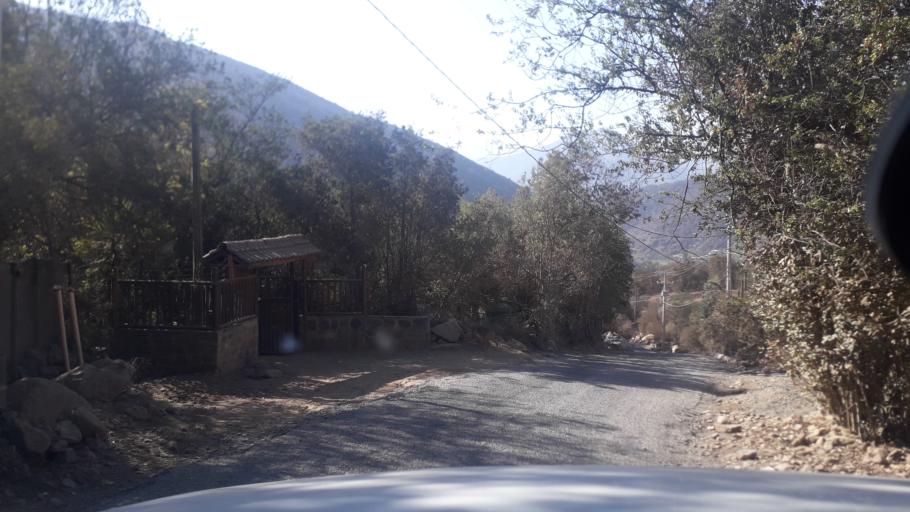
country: CL
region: Valparaiso
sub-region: Provincia de Marga Marga
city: Limache
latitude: -33.0758
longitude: -71.0992
